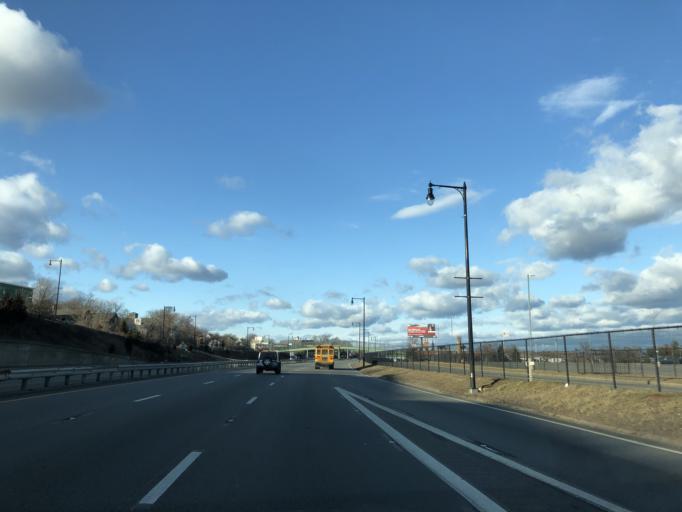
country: US
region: Massachusetts
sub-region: Bristol County
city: New Bedford
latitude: 41.6419
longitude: -70.9262
